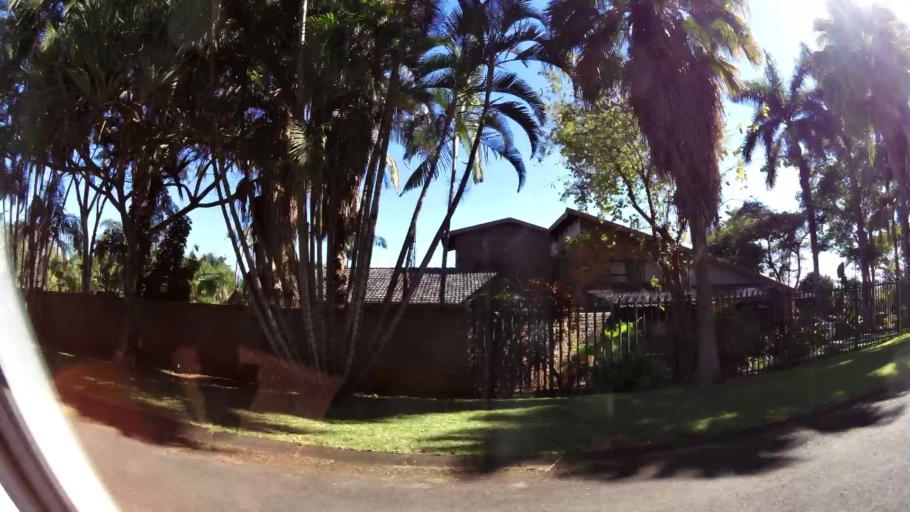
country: ZA
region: Limpopo
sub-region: Mopani District Municipality
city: Tzaneen
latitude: -23.8409
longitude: 30.1452
